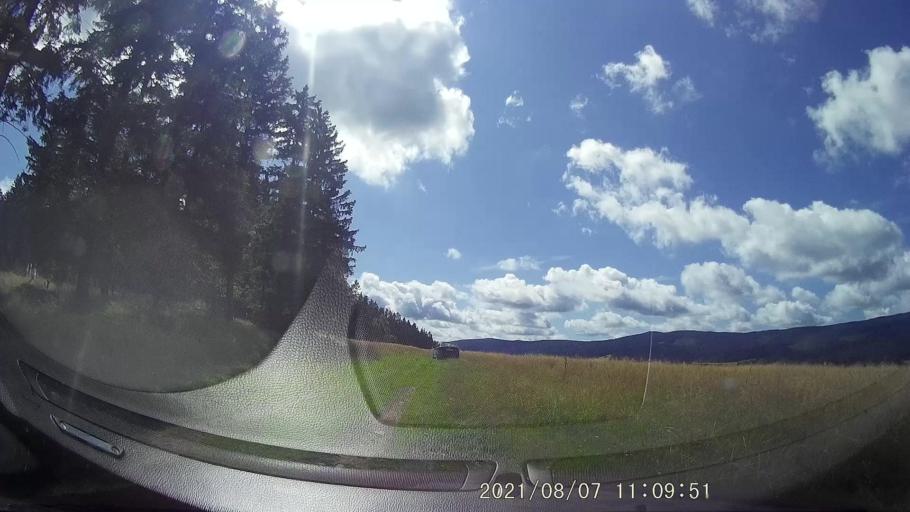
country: CZ
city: Rokytnice v Orlickych Horach
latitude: 50.2735
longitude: 16.4931
